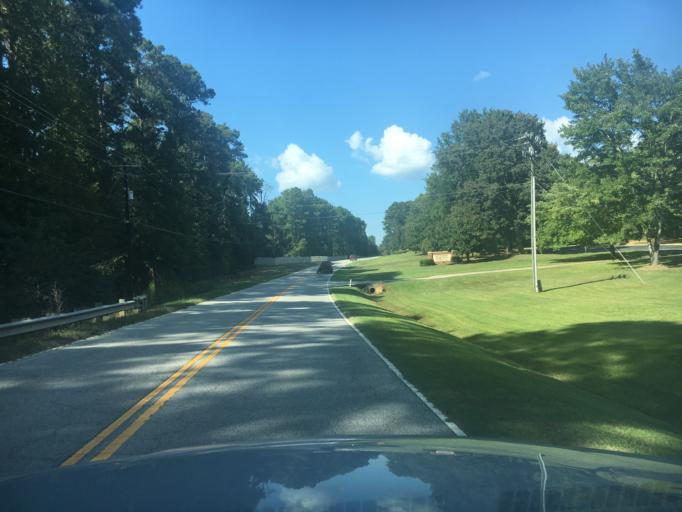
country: US
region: South Carolina
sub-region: Greenwood County
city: Greenwood
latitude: 34.2411
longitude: -82.1811
